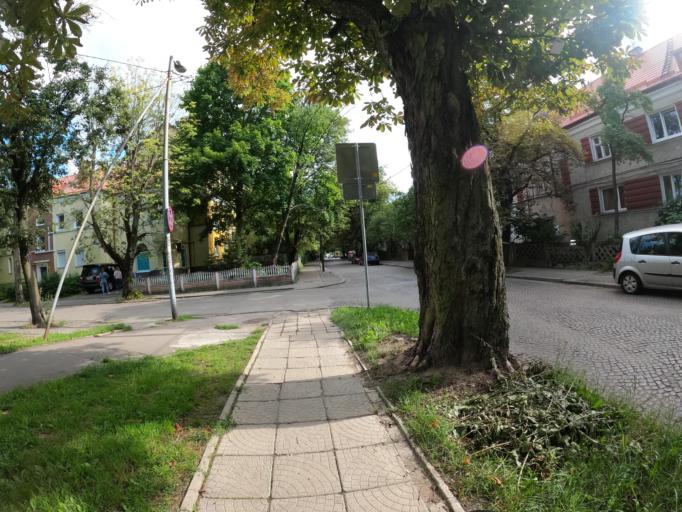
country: RU
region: Kaliningrad
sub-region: Gorod Kaliningrad
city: Kaliningrad
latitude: 54.7276
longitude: 20.4687
